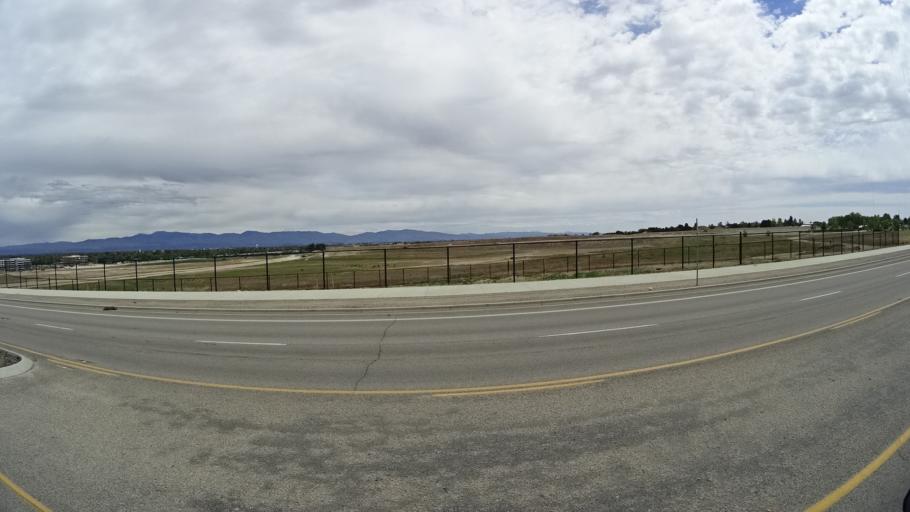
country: US
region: Idaho
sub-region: Ada County
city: Meridian
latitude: 43.5903
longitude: -116.4343
